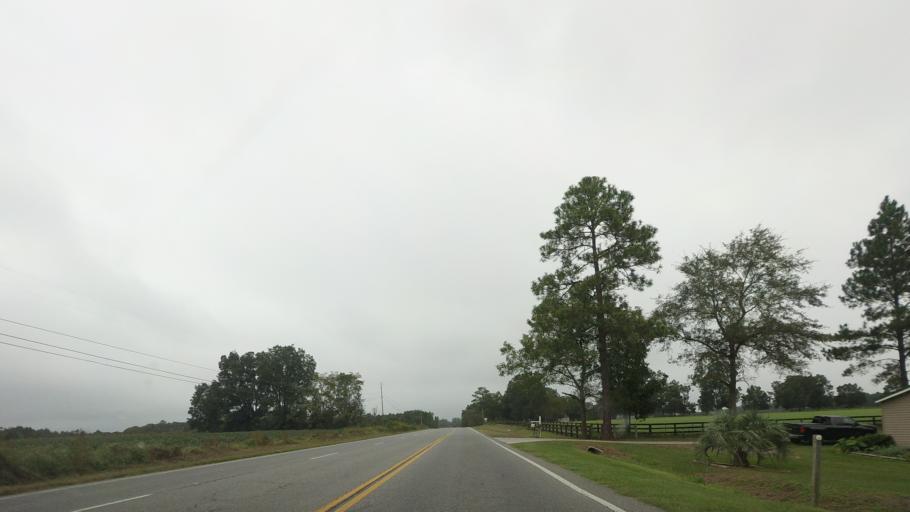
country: US
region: Georgia
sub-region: Ben Hill County
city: Fitzgerald
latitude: 31.6730
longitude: -83.2358
